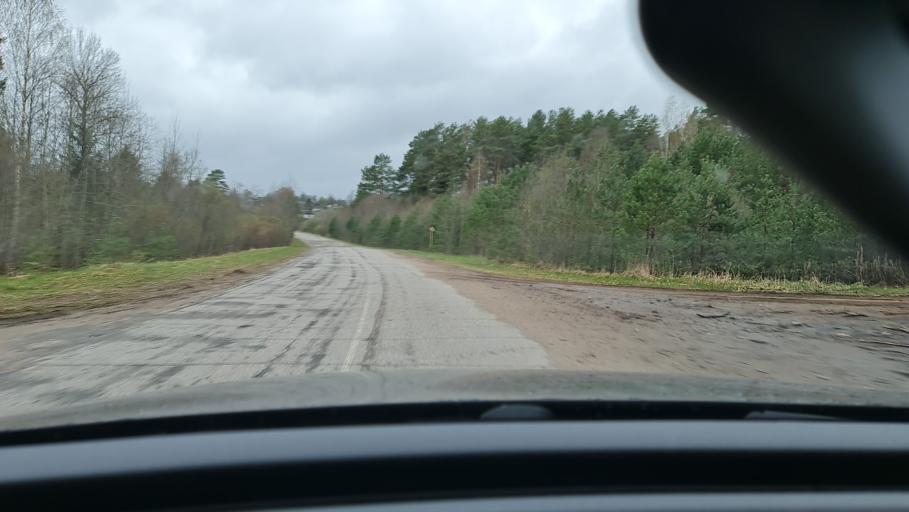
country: RU
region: Novgorod
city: Marevo
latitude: 57.1009
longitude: 31.7244
